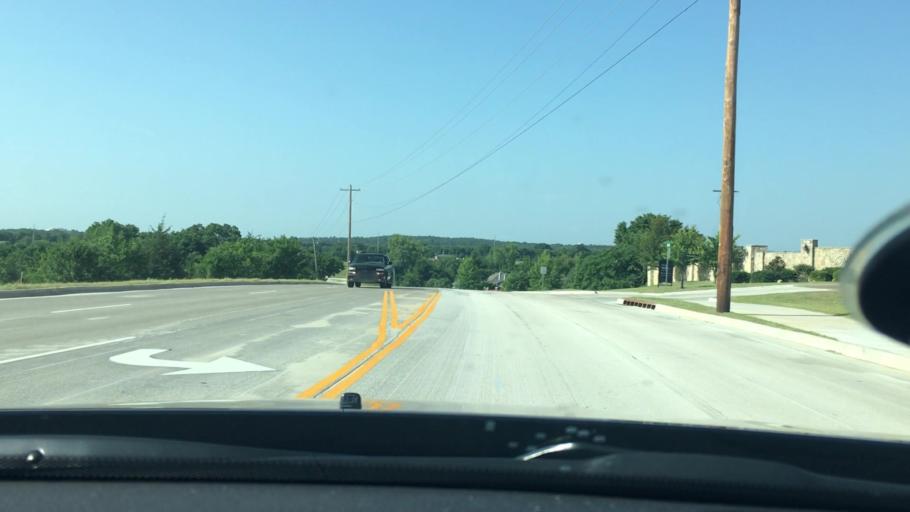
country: US
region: Oklahoma
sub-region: Pontotoc County
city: Ada
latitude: 34.7572
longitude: -96.6697
